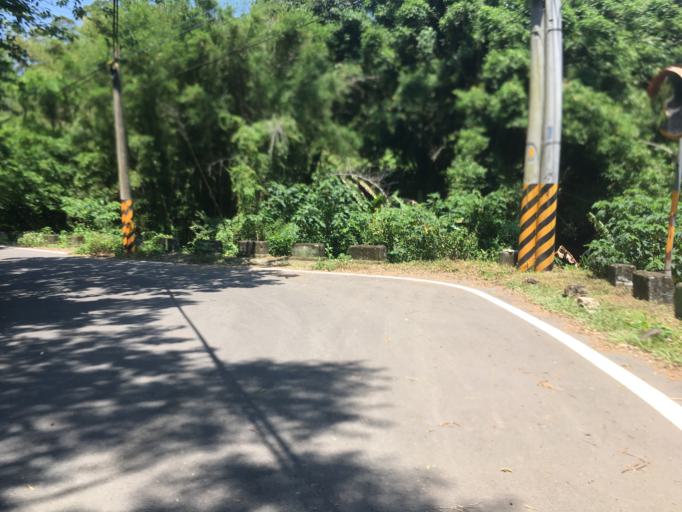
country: TW
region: Taiwan
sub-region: Hsinchu
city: Hsinchu
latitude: 24.7324
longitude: 120.9803
